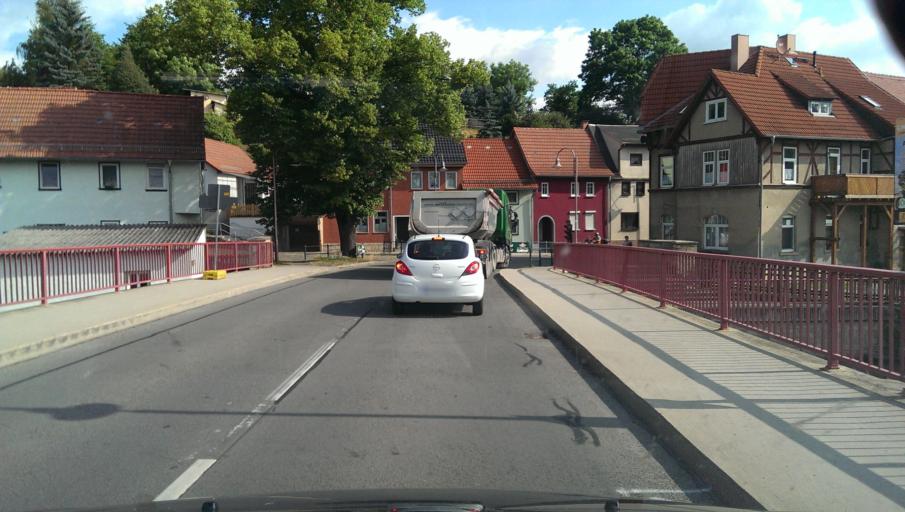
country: DE
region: Thuringia
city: Kranichfeld
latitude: 50.8508
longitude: 11.1984
